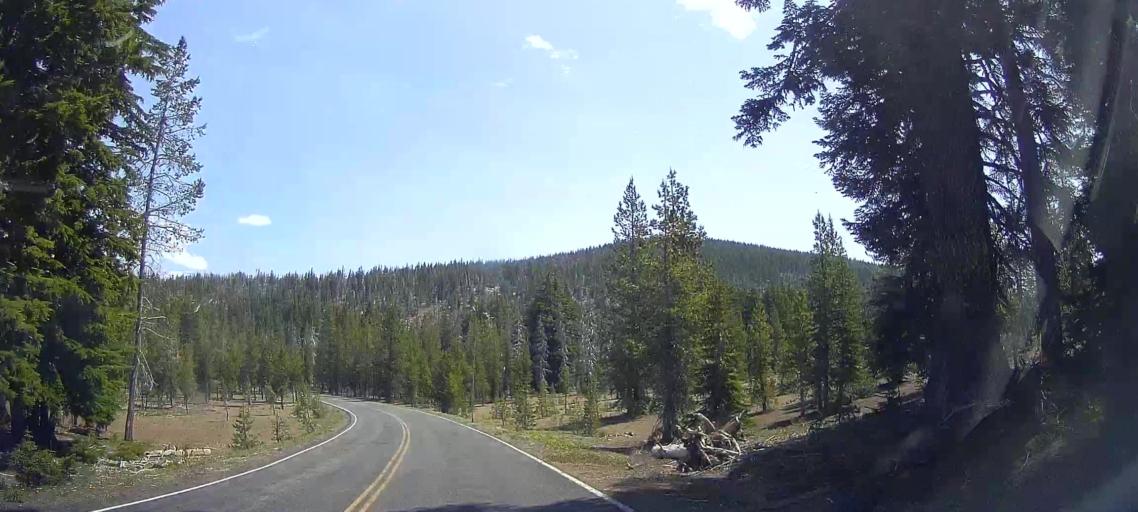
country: US
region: Oregon
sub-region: Jackson County
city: Shady Cove
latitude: 42.9931
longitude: -122.1387
